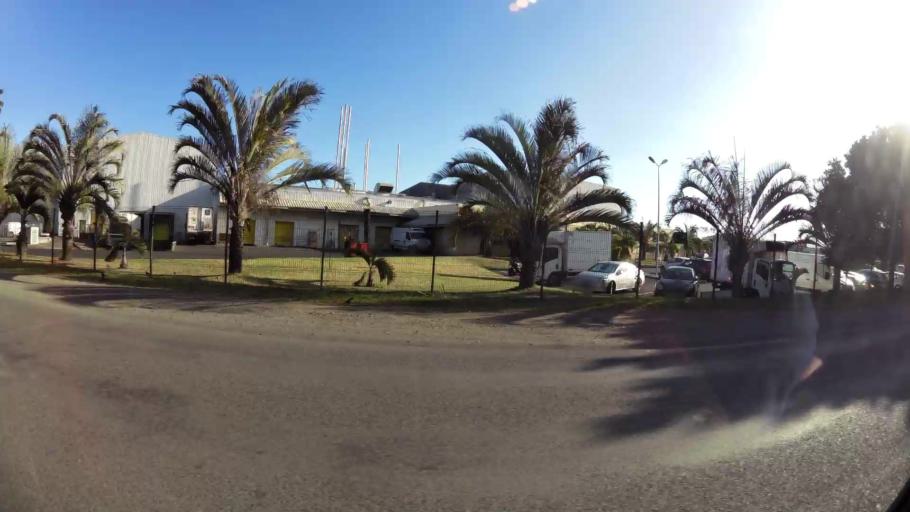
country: RE
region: Reunion
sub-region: Reunion
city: Saint-Louis
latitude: -21.2749
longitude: 55.3726
